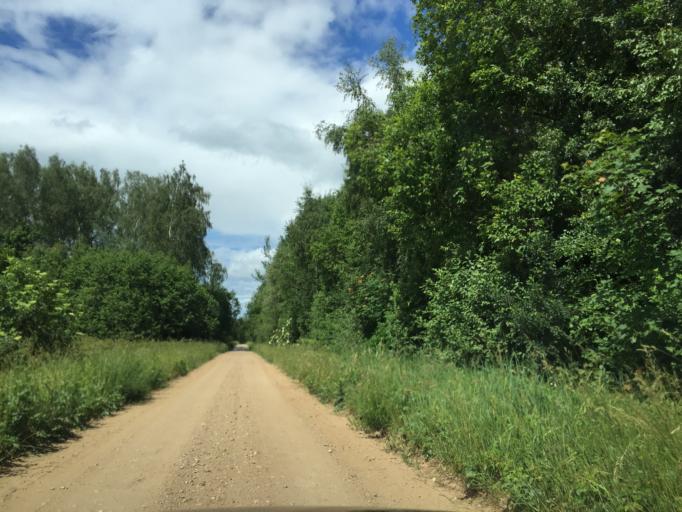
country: LV
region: Lecava
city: Iecava
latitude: 56.5555
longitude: 24.1445
